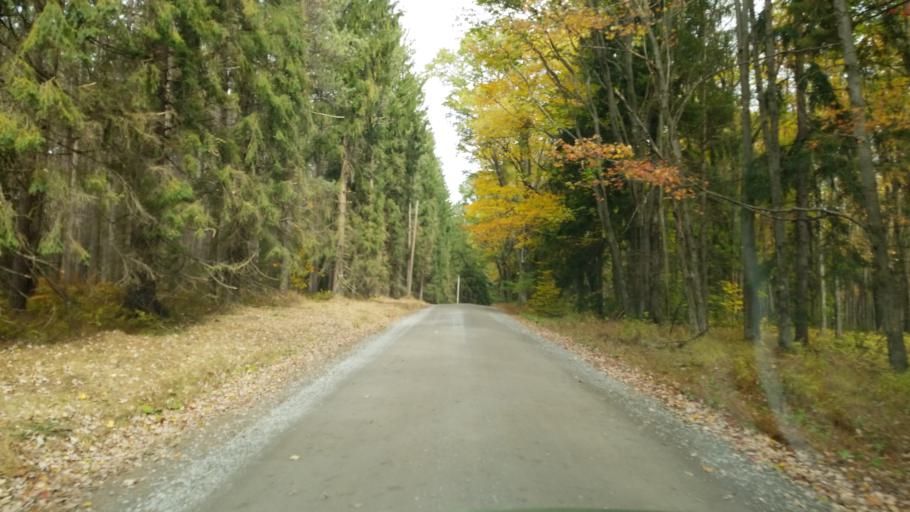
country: US
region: Pennsylvania
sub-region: Clearfield County
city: Clearfield
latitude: 41.1895
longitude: -78.4428
